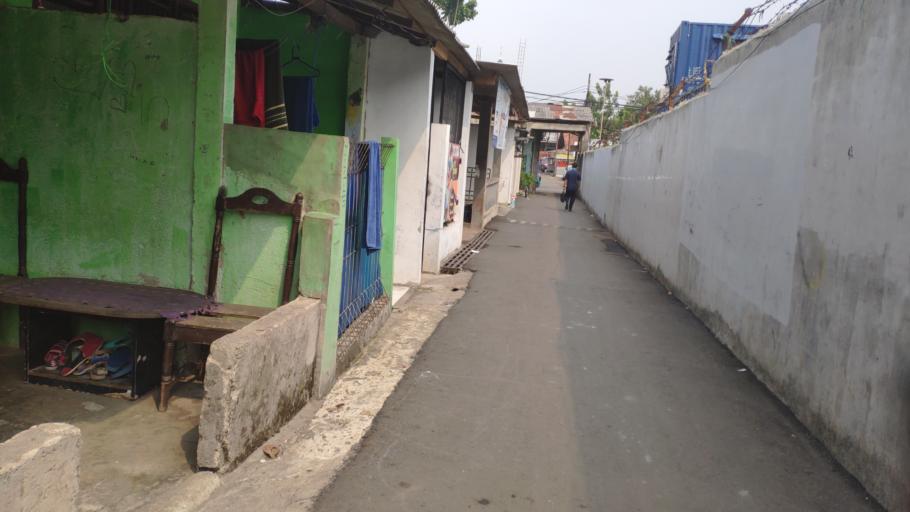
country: ID
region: West Java
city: Depok
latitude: -6.3460
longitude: 106.8145
